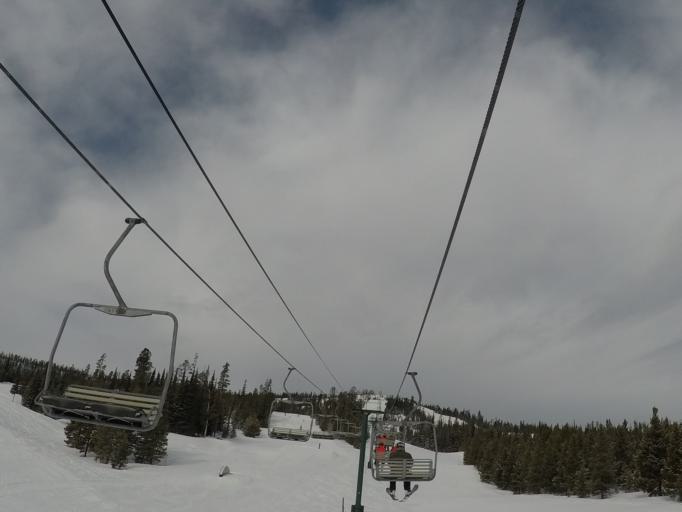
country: US
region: Montana
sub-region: Meagher County
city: White Sulphur Springs
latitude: 46.8360
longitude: -110.7015
